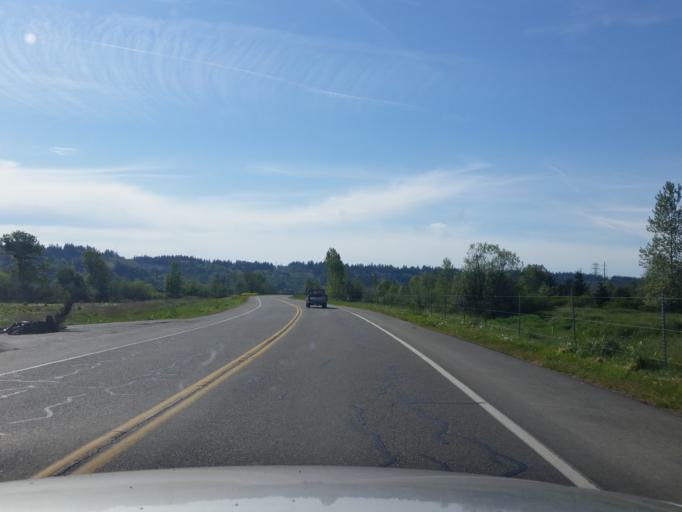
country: US
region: Washington
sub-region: Snohomish County
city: Fobes Hill
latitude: 47.9242
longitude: -122.1576
